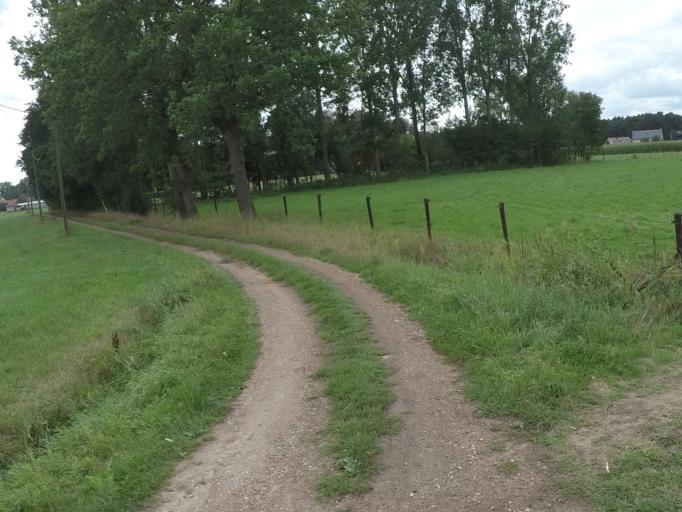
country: BE
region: Flanders
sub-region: Provincie Antwerpen
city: Vorselaar
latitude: 51.2264
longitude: 4.7575
